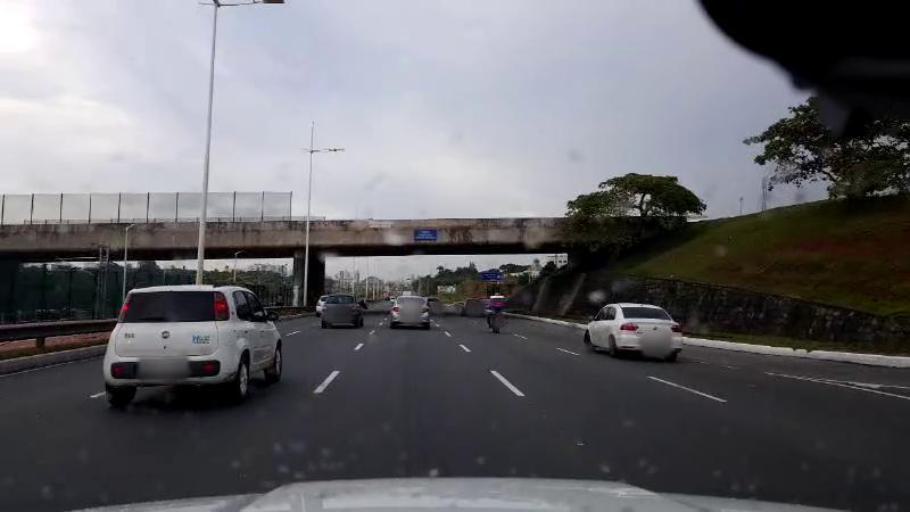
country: BR
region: Bahia
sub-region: Salvador
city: Salvador
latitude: -12.9490
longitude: -38.4245
